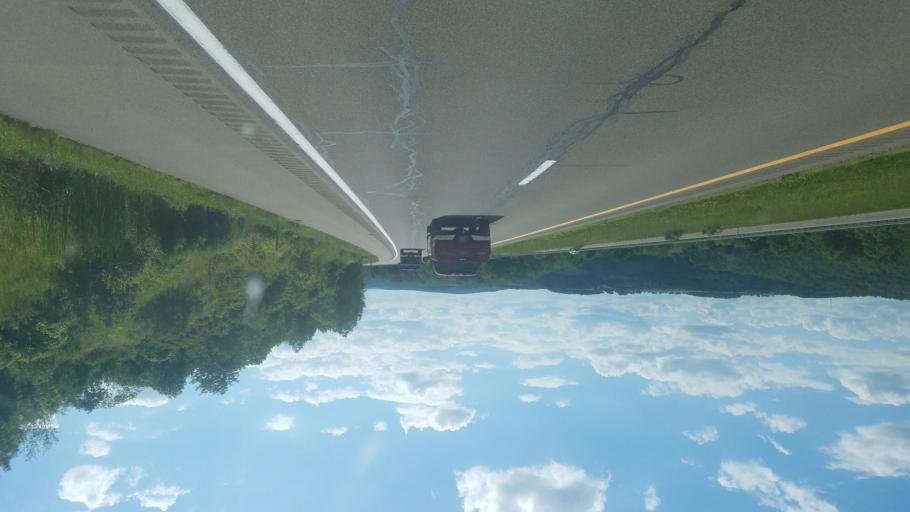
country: US
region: New York
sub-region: Steuben County
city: Hornell
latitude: 42.3757
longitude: -77.5571
